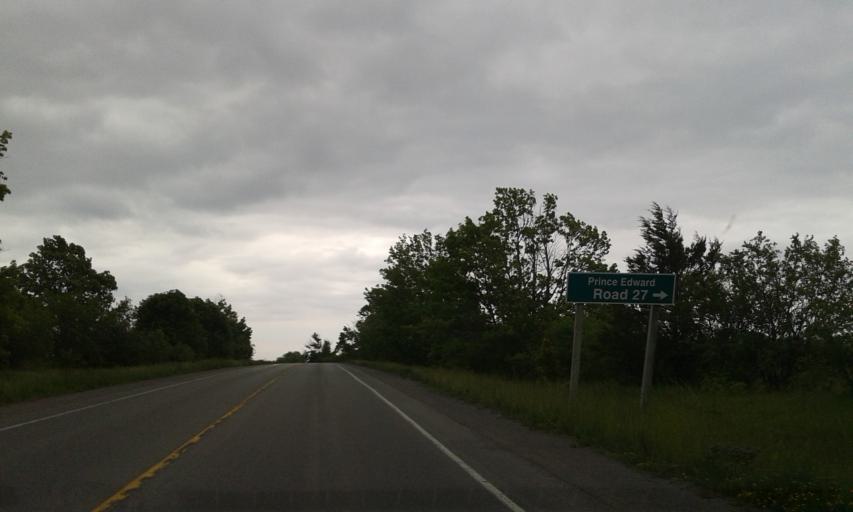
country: CA
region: Ontario
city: Quinte West
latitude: 43.9657
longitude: -77.5006
